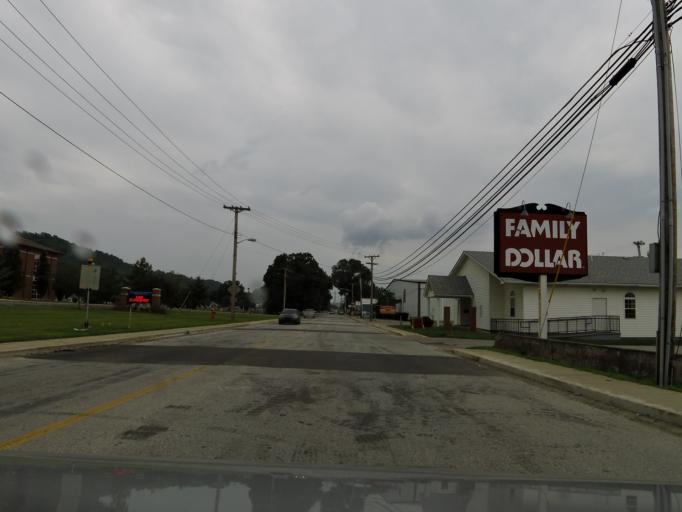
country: US
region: Ohio
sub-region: Brown County
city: Ripley
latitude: 38.7372
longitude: -83.8402
